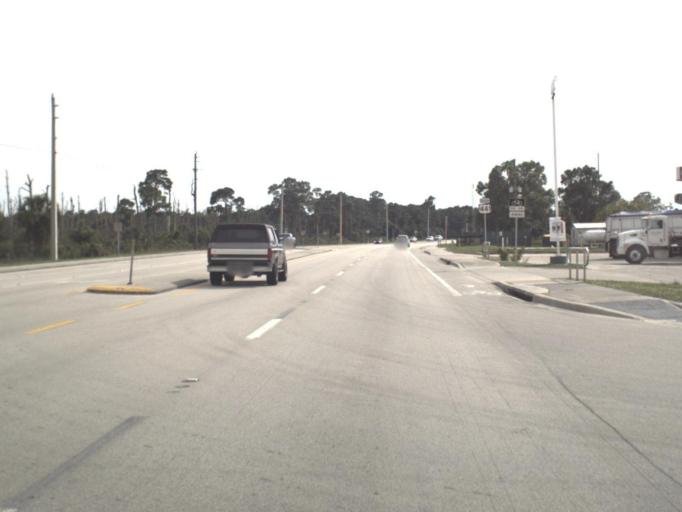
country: US
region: Florida
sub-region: Okeechobee County
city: Cypress Quarters
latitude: 27.2783
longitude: -80.8289
